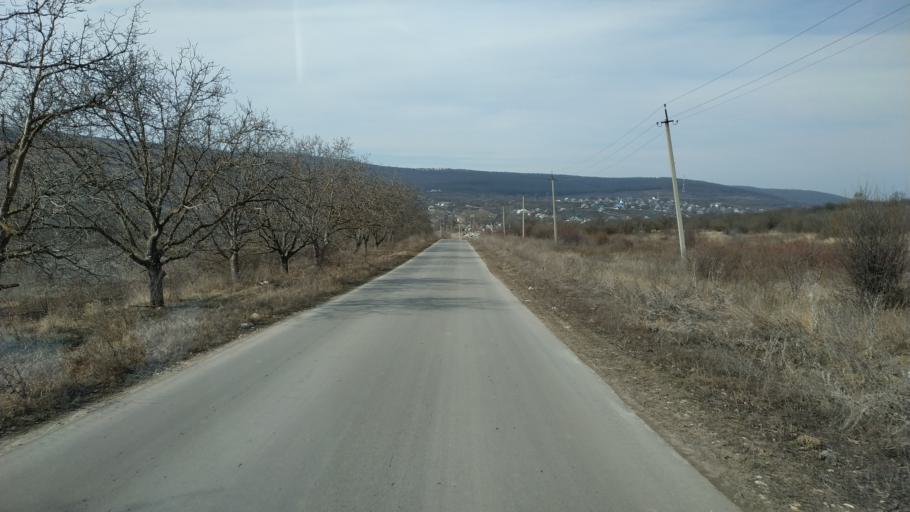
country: MD
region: Nisporeni
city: Nisporeni
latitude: 47.1466
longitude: 28.1187
